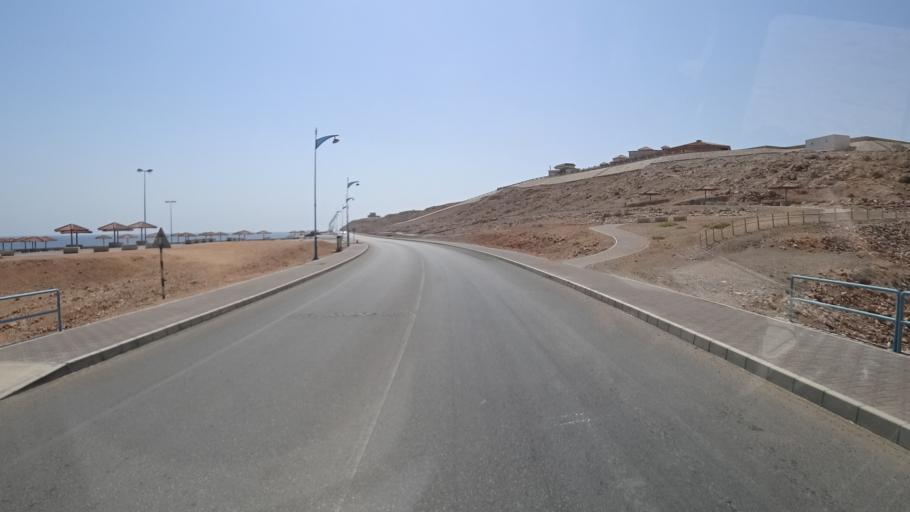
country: OM
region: Ash Sharqiyah
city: Sur
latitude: 22.5666
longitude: 59.5578
